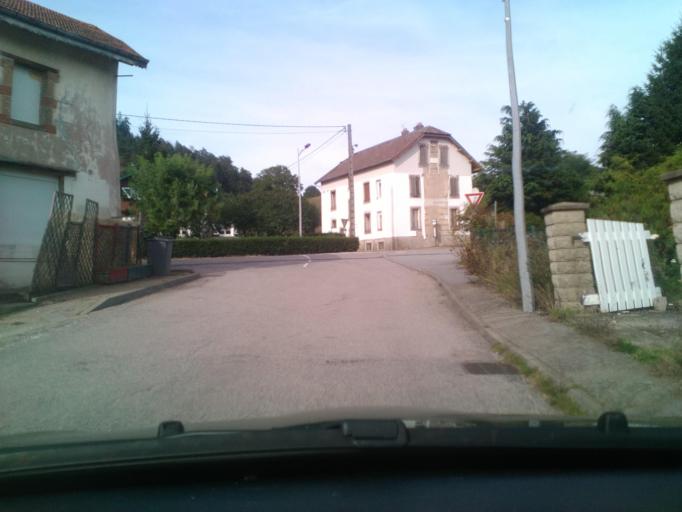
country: FR
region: Lorraine
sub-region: Departement des Vosges
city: Corcieux
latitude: 48.2000
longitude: 6.8778
